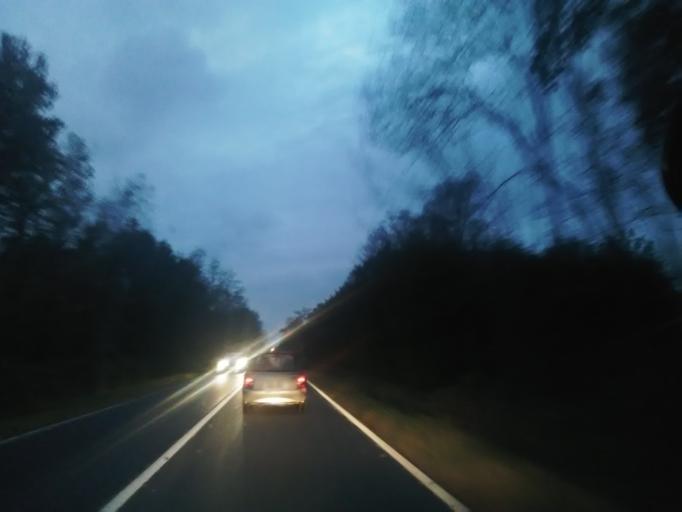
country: IT
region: Piedmont
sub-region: Provincia di Vercelli
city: Lozzolo
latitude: 45.6105
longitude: 8.3388
